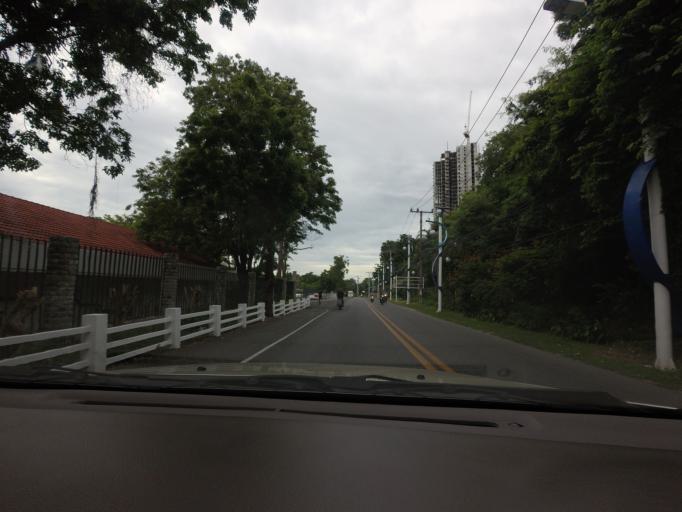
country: TH
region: Chon Buri
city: Phatthaya
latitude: 12.9226
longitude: 100.8651
